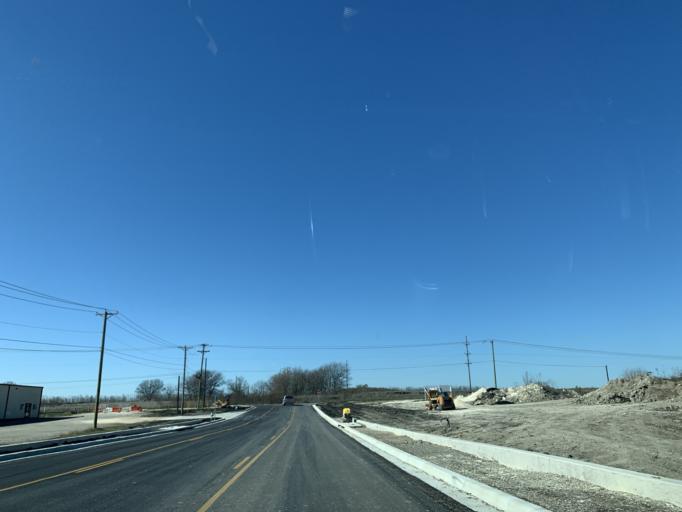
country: US
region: Texas
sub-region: Williamson County
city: Hutto
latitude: 30.5486
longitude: -97.5713
